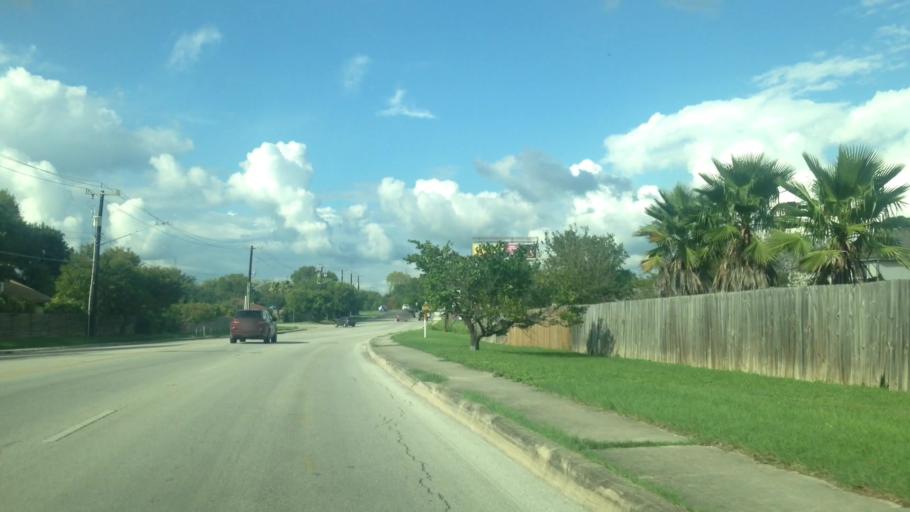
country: US
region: Texas
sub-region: Bexar County
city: Windcrest
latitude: 29.5699
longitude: -98.4194
